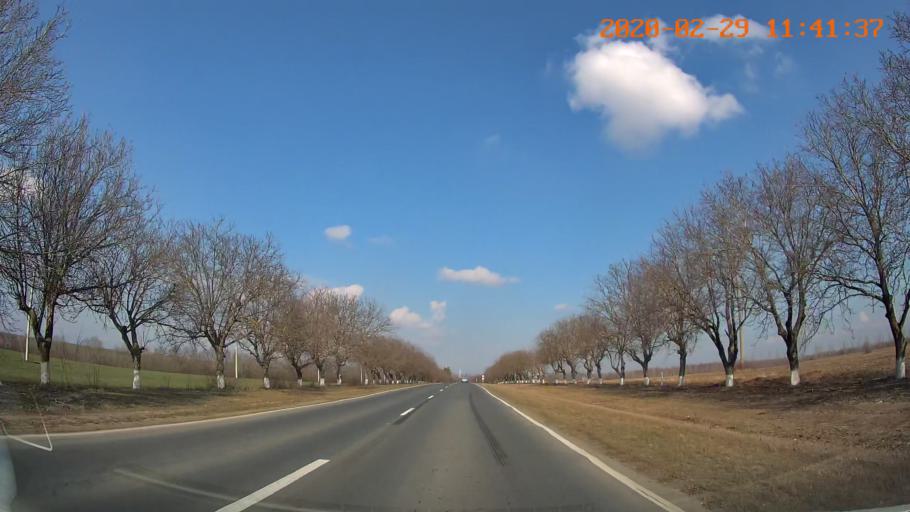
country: MD
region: Rezina
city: Saharna
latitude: 47.6741
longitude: 29.0158
